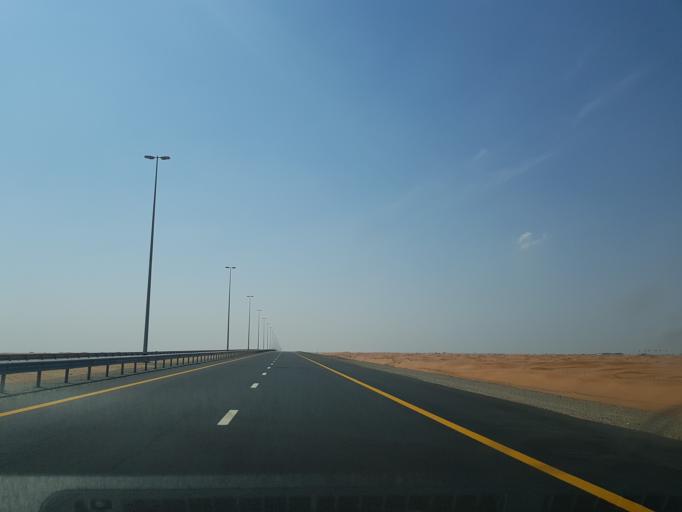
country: AE
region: Ash Shariqah
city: Adh Dhayd
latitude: 25.2532
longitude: 55.7647
